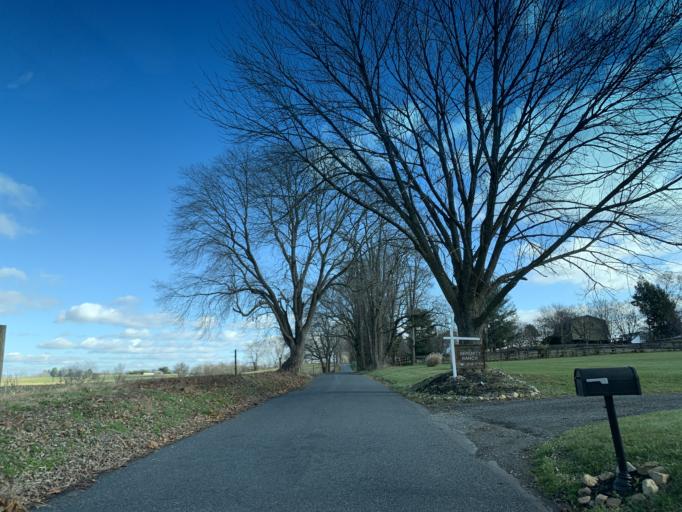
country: US
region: Maryland
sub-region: Harford County
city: South Bel Air
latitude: 39.5825
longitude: -76.2466
